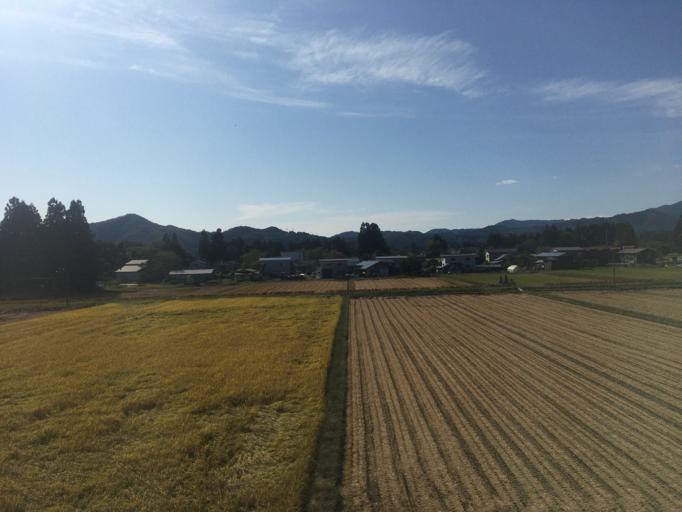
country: JP
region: Akita
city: Kakunodatemachi
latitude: 39.6209
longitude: 140.5748
